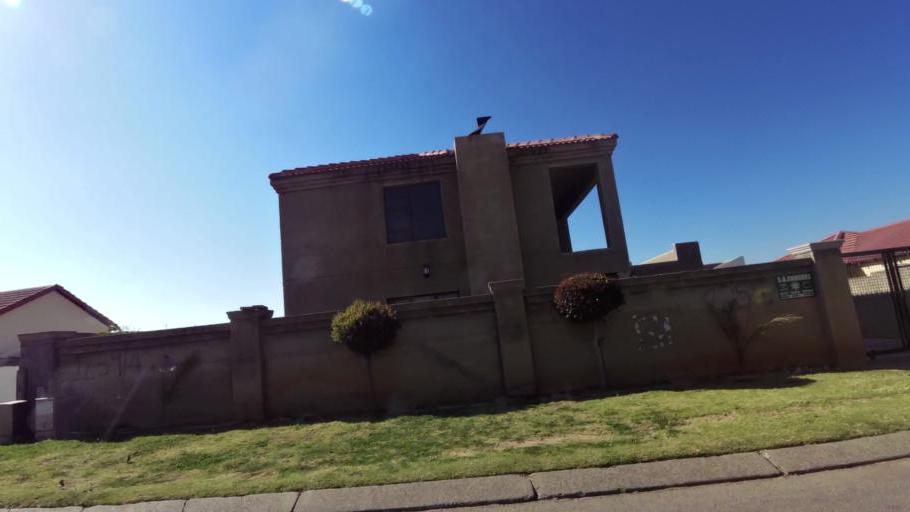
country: ZA
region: Gauteng
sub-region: City of Johannesburg Metropolitan Municipality
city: Johannesburg
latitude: -26.2511
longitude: 27.9860
